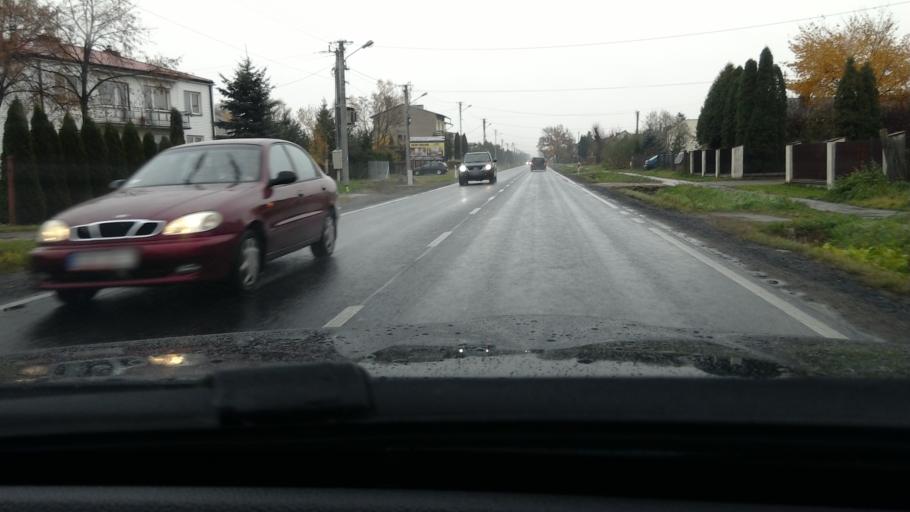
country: PL
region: Lodz Voivodeship
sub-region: Skierniewice
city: Skierniewice
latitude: 51.9926
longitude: 20.1065
